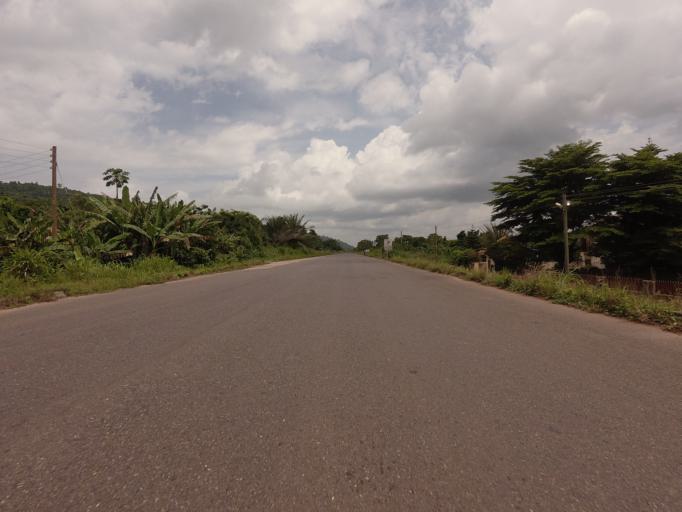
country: GH
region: Volta
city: Ho
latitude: 6.4962
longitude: 0.2032
